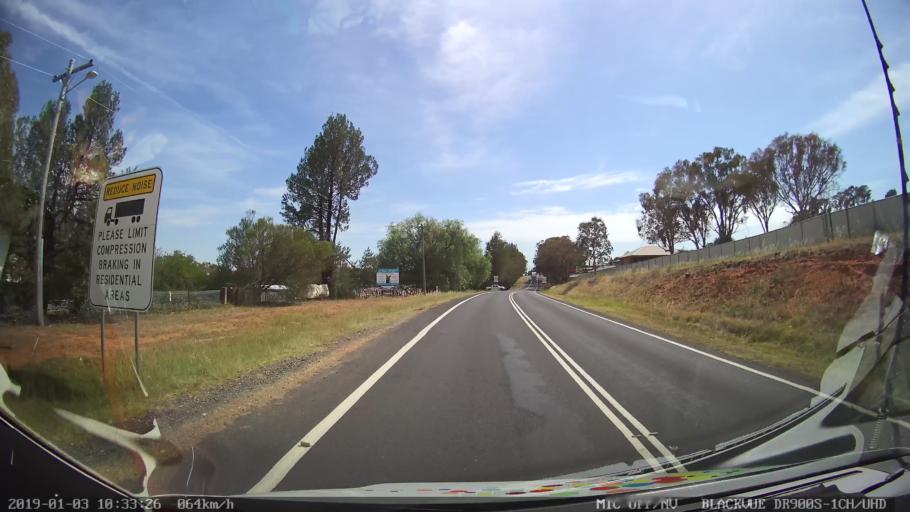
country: AU
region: New South Wales
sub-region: Young
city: Young
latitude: -34.3284
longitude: 148.2875
